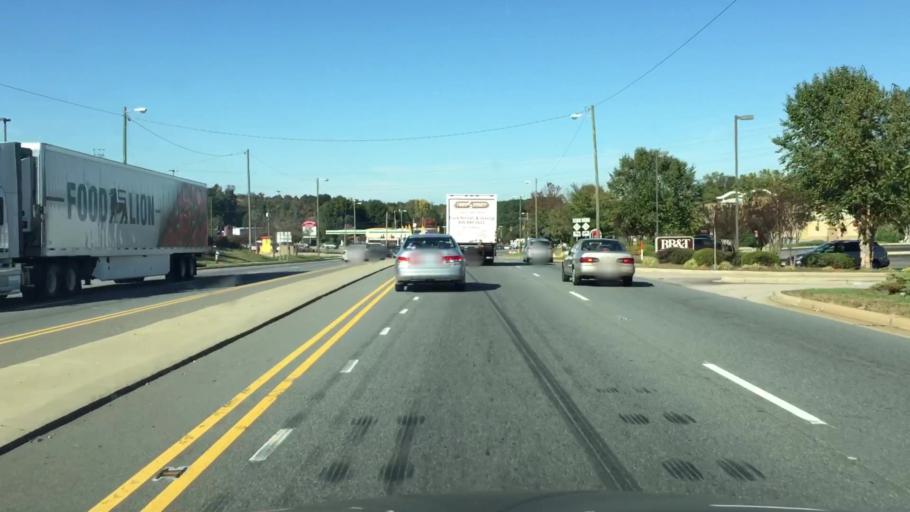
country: US
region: North Carolina
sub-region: Rowan County
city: Salisbury
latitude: 35.6598
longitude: -80.5004
